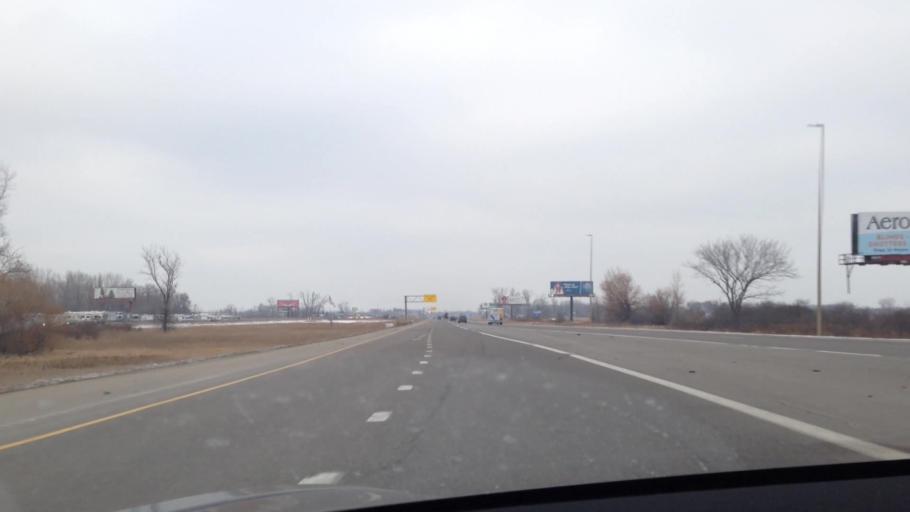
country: US
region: Minnesota
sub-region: Anoka County
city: Columbus
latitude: 45.2223
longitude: -93.0274
